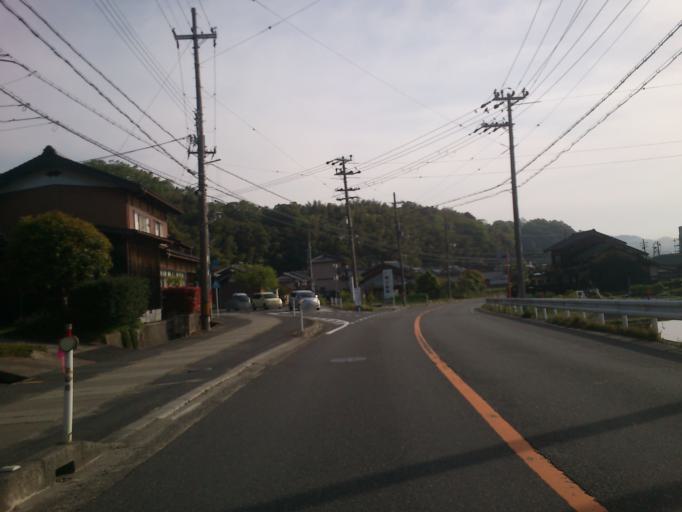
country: JP
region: Kyoto
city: Miyazu
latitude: 35.5603
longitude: 135.1414
